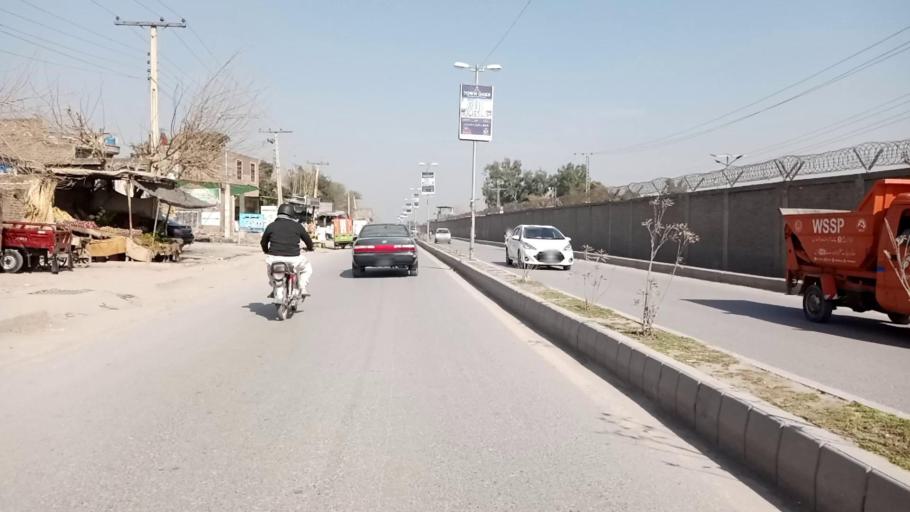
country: PK
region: Khyber Pakhtunkhwa
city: Peshawar
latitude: 33.9767
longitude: 71.5147
